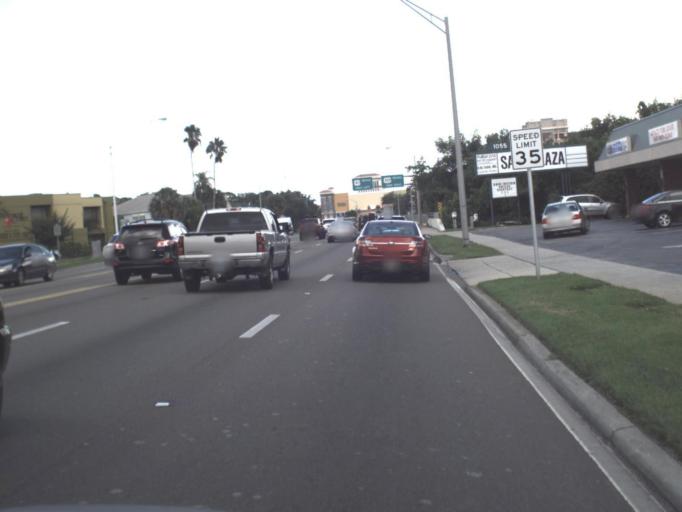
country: US
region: Florida
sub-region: Sarasota County
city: Sarasota
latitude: 27.3234
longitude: -82.5296
